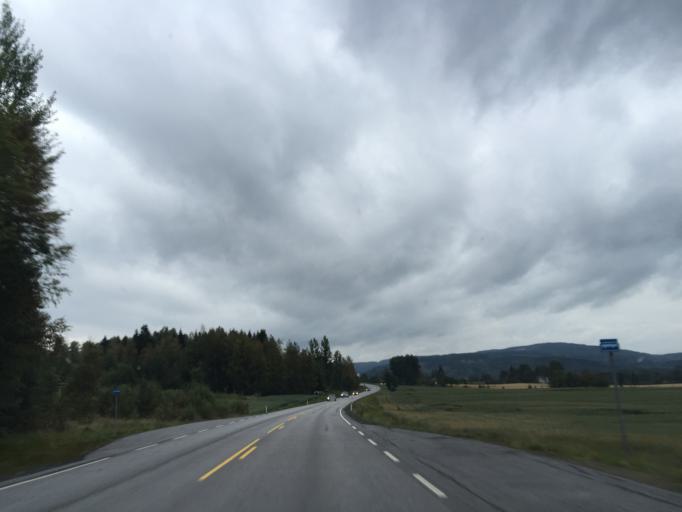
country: NO
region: Hedmark
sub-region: Nord-Odal
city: Sand
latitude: 60.4260
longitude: 11.5133
